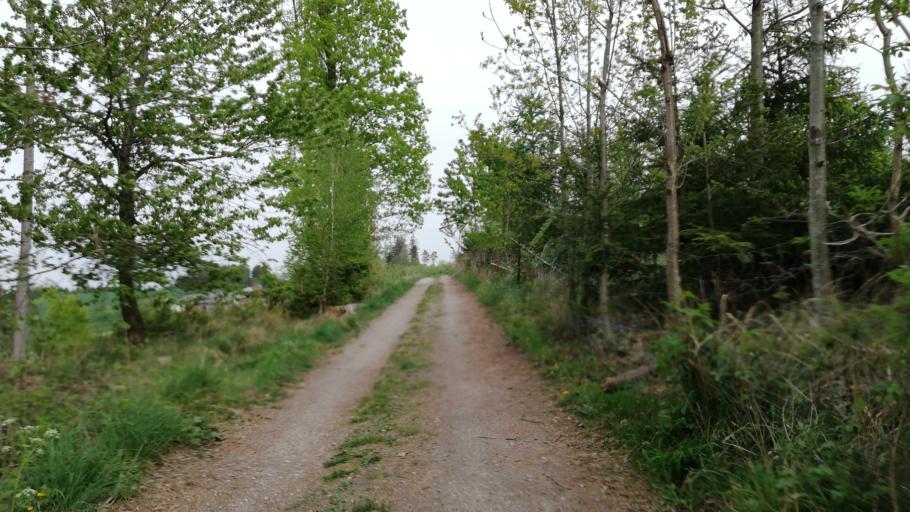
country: AT
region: Upper Austria
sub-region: Wels-Land
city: Gunskirchen
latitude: 48.1822
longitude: 13.9524
